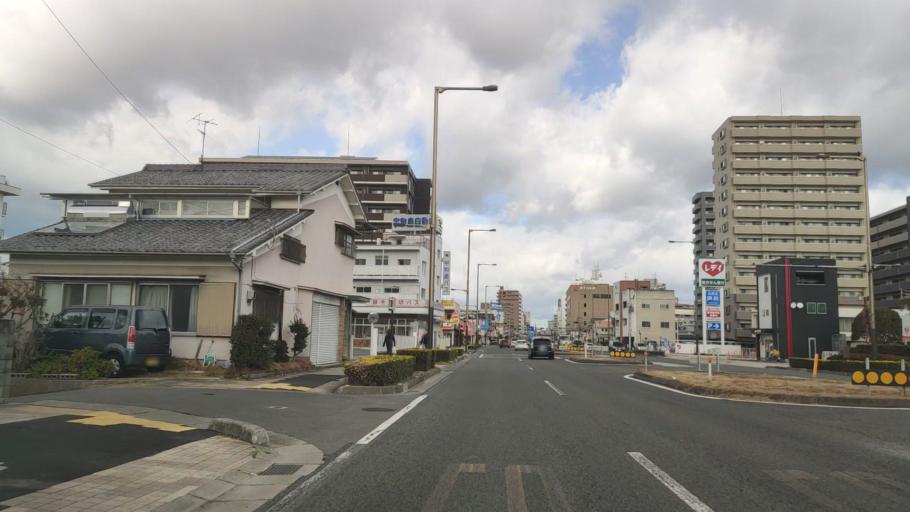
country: JP
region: Ehime
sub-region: Shikoku-chuo Shi
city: Matsuyama
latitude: 33.8321
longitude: 132.7587
